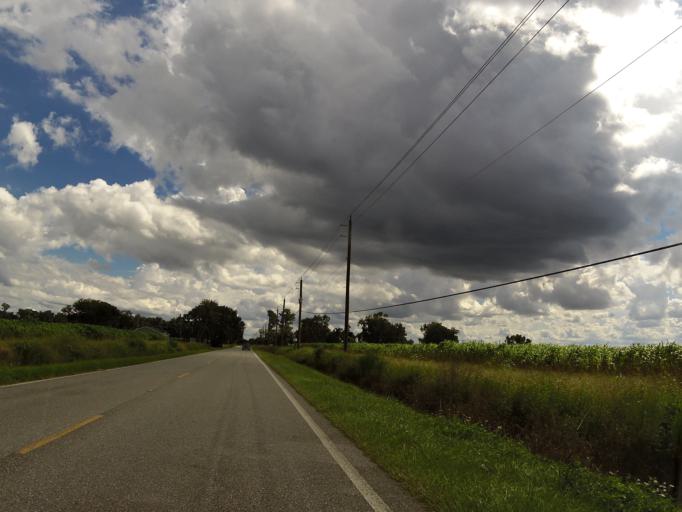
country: US
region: Florida
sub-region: Saint Johns County
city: Saint Augustine Shores
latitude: 29.8013
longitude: -81.4846
